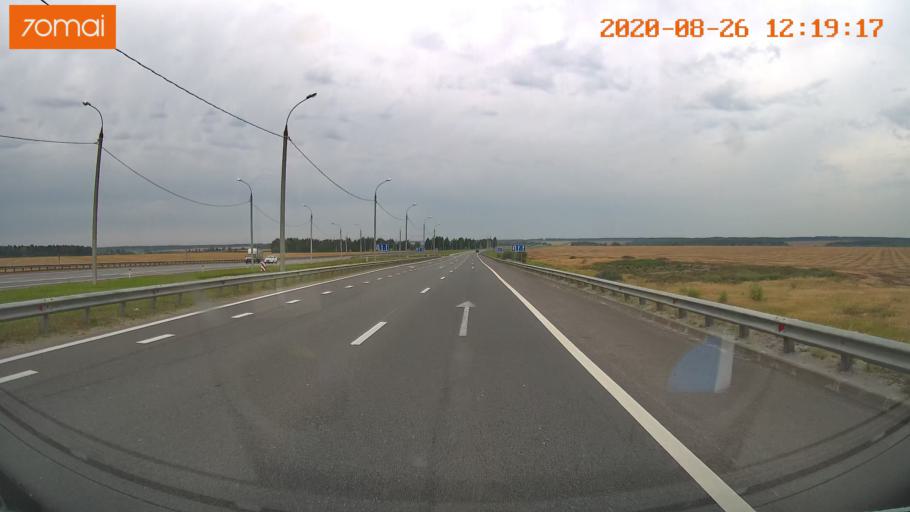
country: RU
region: Rjazan
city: Murmino
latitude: 54.4743
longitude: 40.0013
